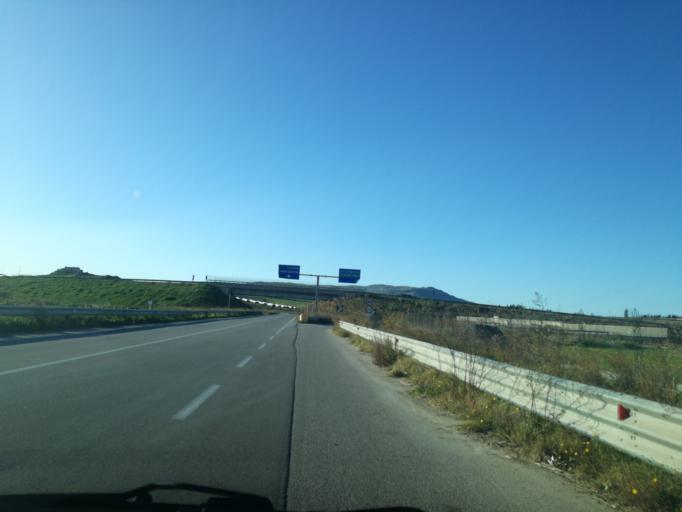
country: IT
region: Sicily
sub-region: Provincia di Caltanissetta
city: Butera
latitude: 37.1252
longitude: 14.1206
